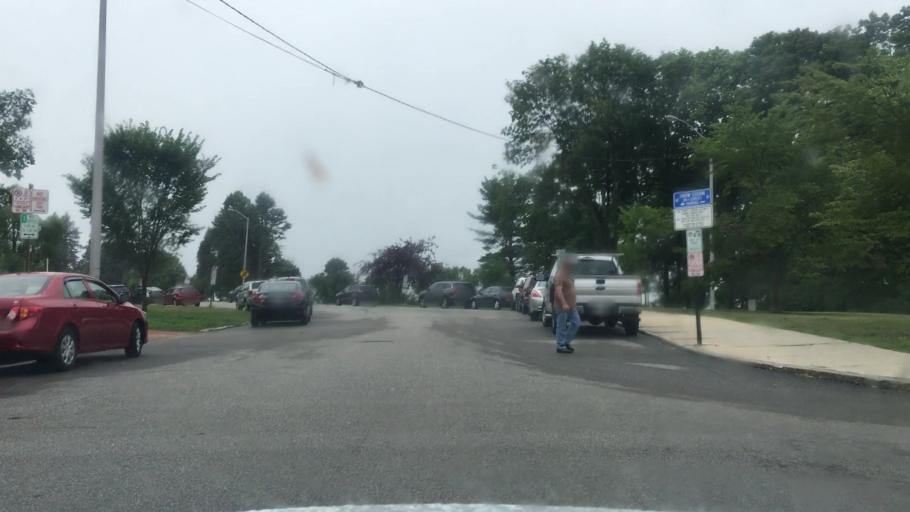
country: US
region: Maine
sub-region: Cumberland County
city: Portland
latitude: 43.6519
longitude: -70.2756
